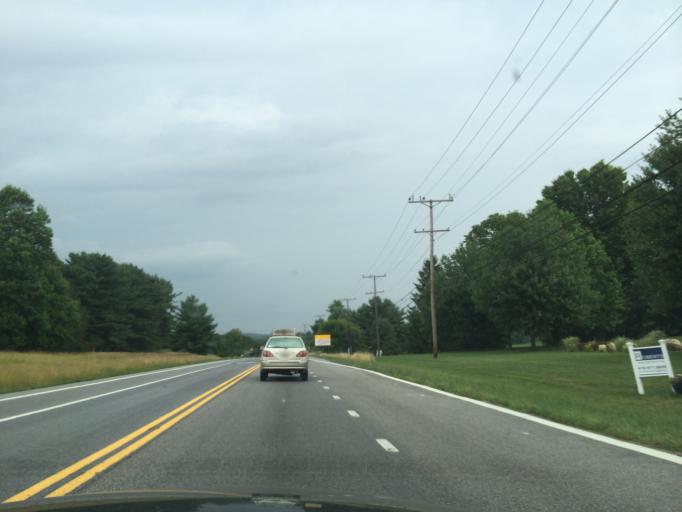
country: US
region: Maryland
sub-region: Carroll County
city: Sykesville
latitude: 39.3380
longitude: -76.9530
